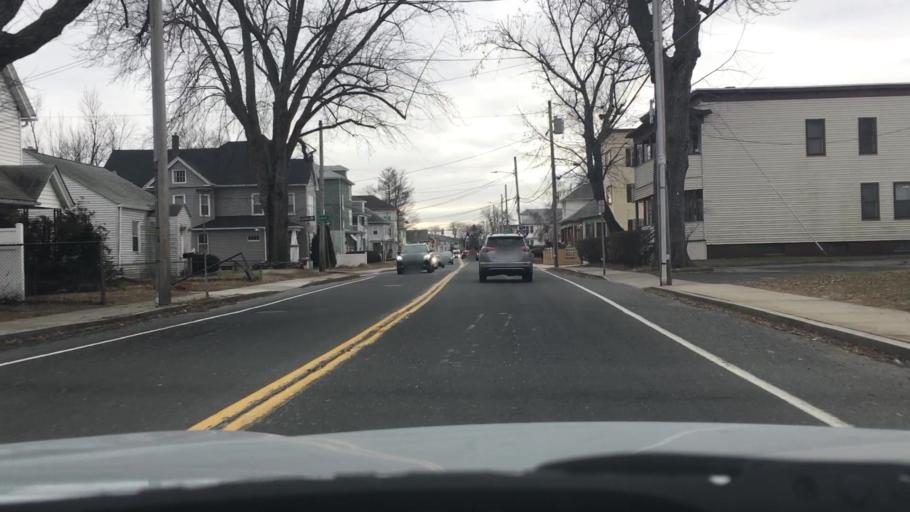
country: US
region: Massachusetts
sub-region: Hampden County
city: North Chicopee
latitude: 42.1846
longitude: -72.6100
